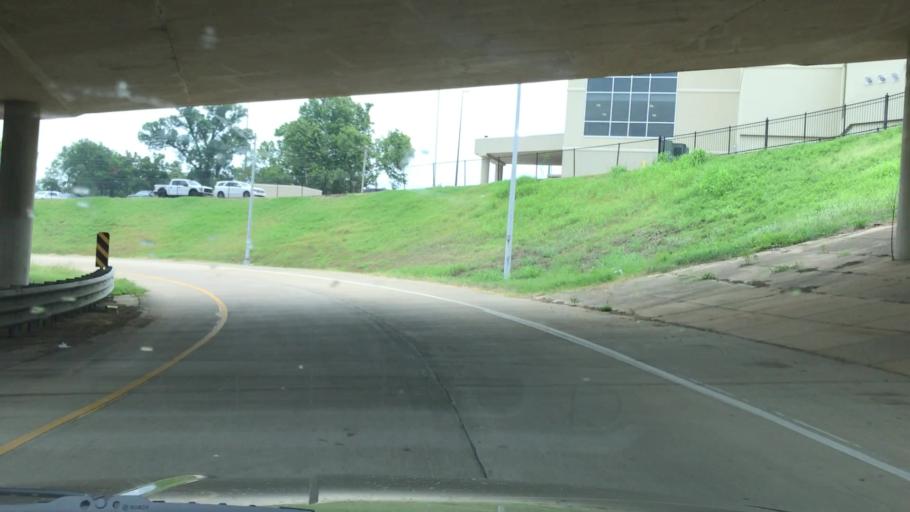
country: US
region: Louisiana
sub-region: Bossier Parish
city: Bossier City
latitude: 32.5031
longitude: -93.7462
